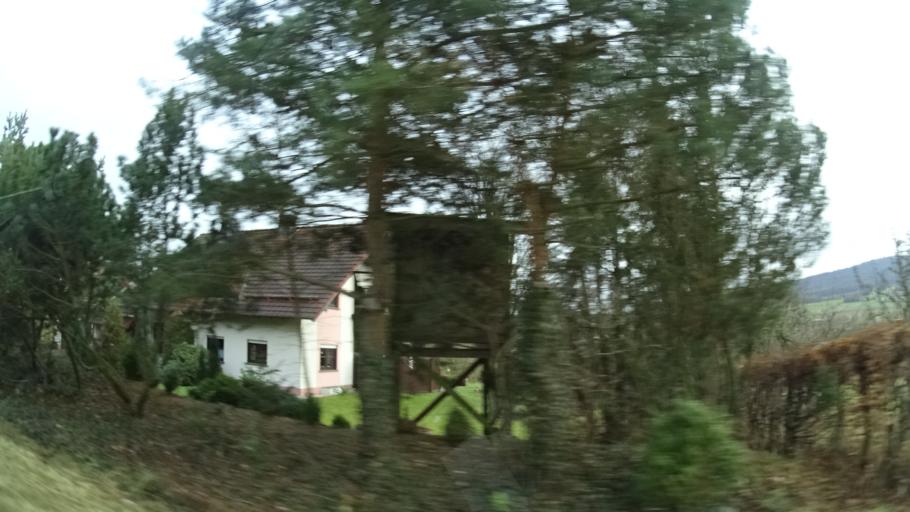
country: DE
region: Hesse
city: Tann
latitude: 50.6231
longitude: 9.9952
